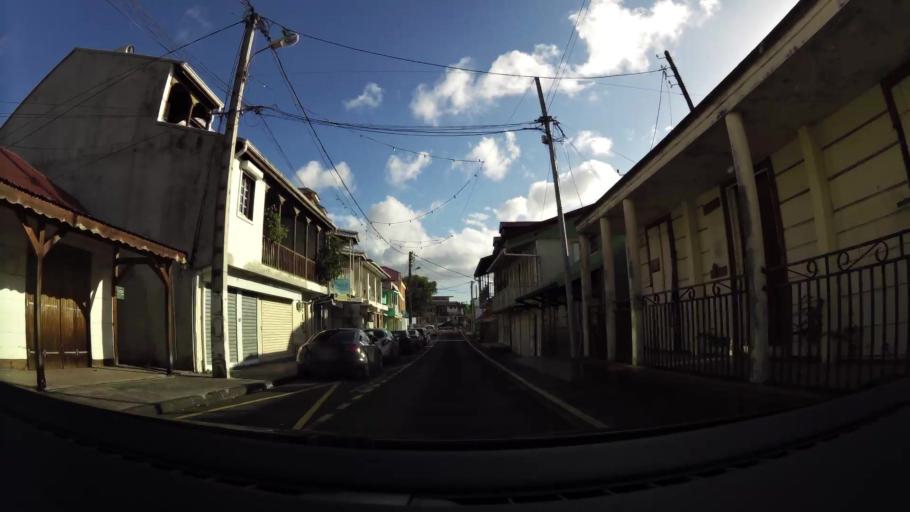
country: GP
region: Guadeloupe
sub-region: Guadeloupe
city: Pointe-Noire
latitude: 16.2342
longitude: -61.7901
